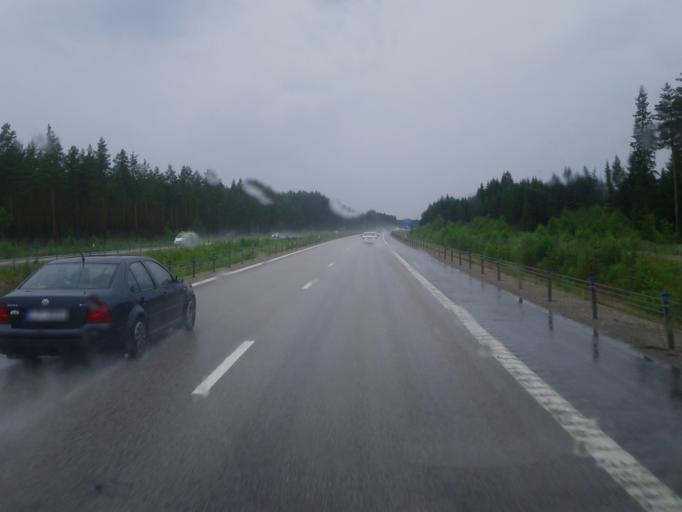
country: SE
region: Uppsala
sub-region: Alvkarleby Kommun
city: AElvkarleby
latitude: 60.4445
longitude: 17.4181
